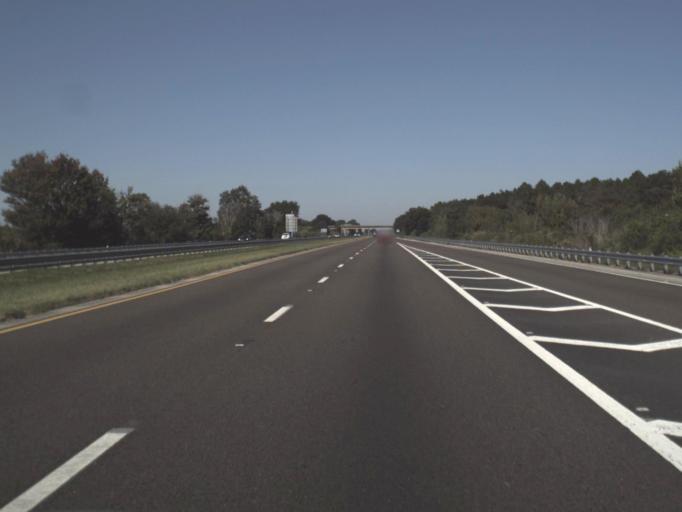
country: US
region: Florida
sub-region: Lake County
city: Yalaha
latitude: 28.6799
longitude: -81.8590
